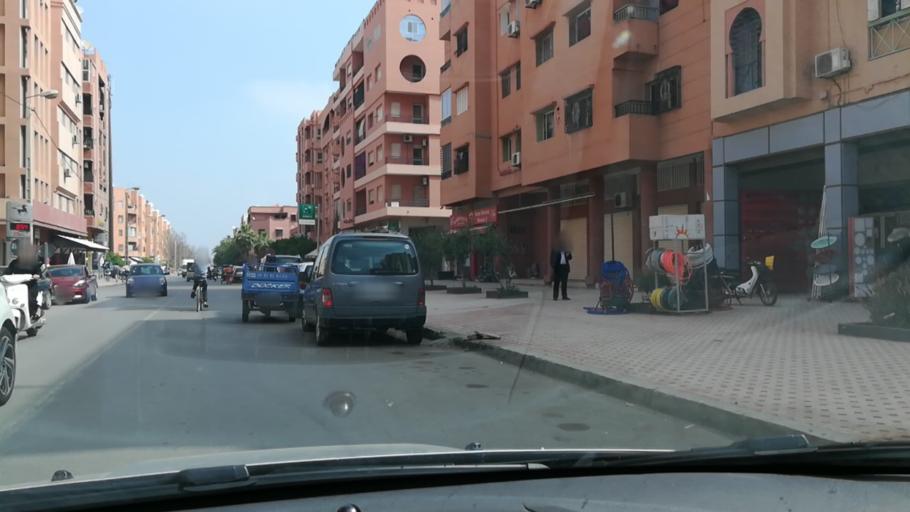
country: MA
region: Marrakech-Tensift-Al Haouz
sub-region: Marrakech
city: Marrakesh
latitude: 31.6302
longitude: -8.0625
